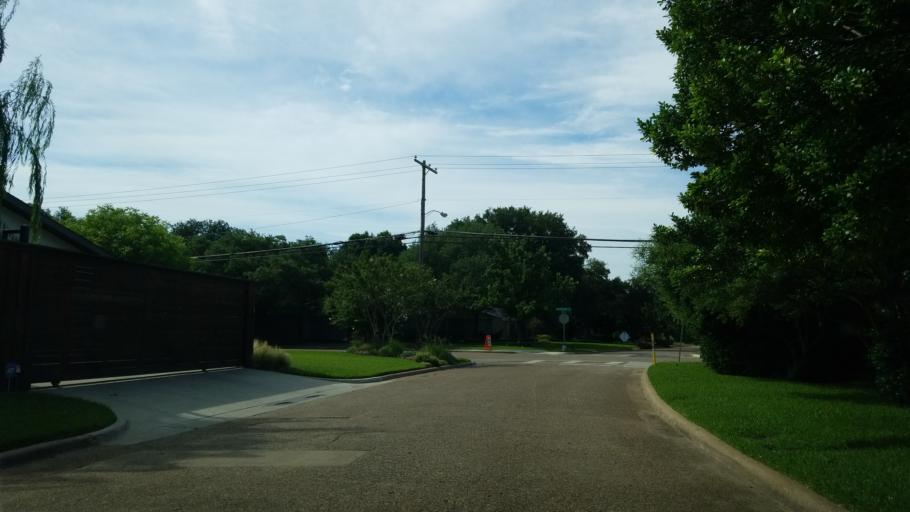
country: US
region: Texas
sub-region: Dallas County
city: Farmers Branch
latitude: 32.9026
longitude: -96.8434
